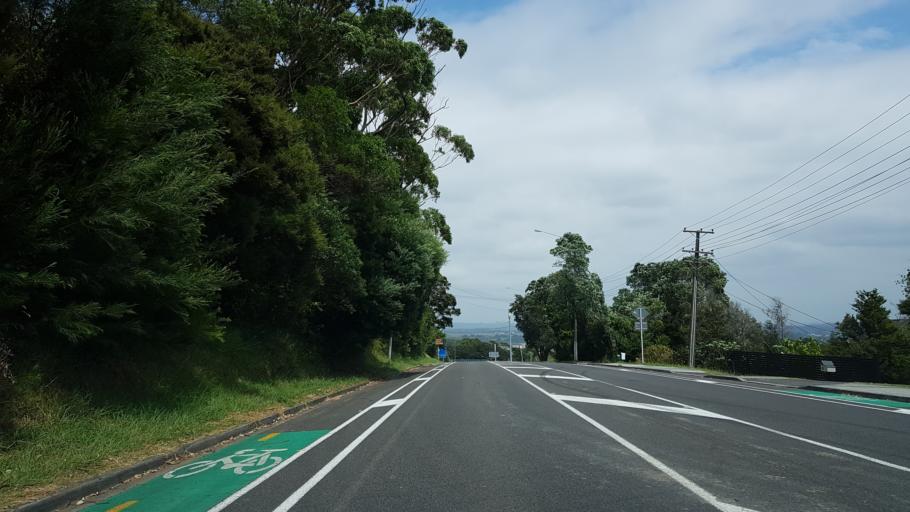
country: NZ
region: Auckland
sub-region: Auckland
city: North Shore
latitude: -36.7803
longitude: 174.6809
